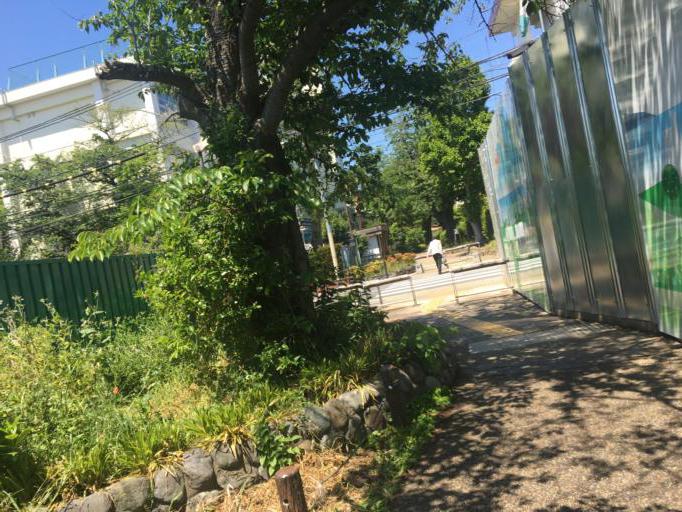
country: JP
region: Saitama
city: Wako
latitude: 35.7671
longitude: 139.6580
